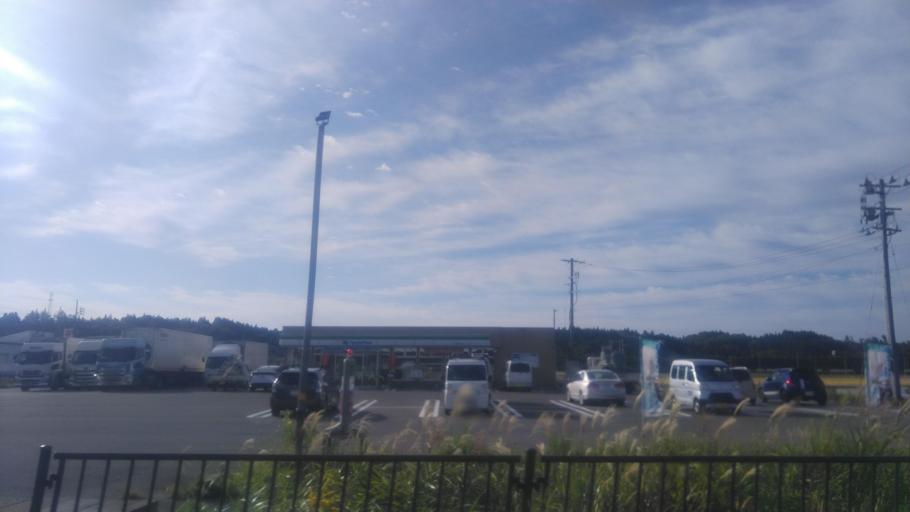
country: JP
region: Akita
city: Noshiromachi
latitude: 40.1886
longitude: 140.0785
